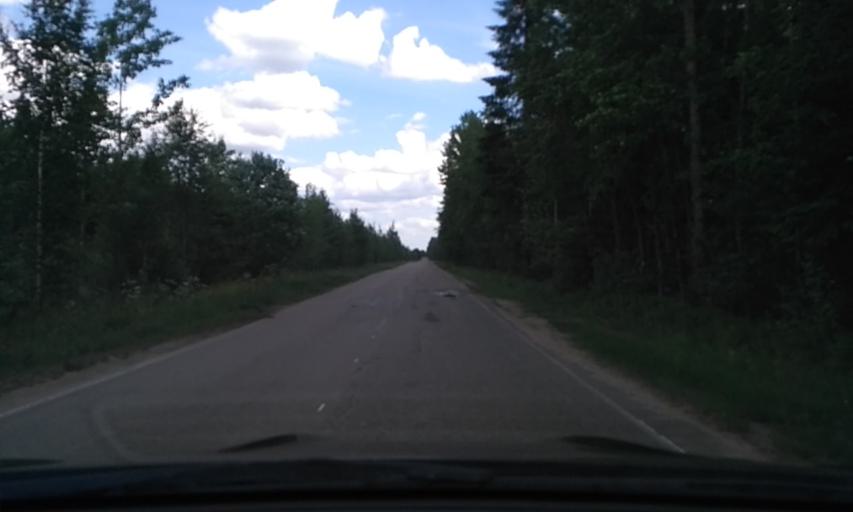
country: RU
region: Leningrad
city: Otradnoye
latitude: 59.8201
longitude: 30.8048
